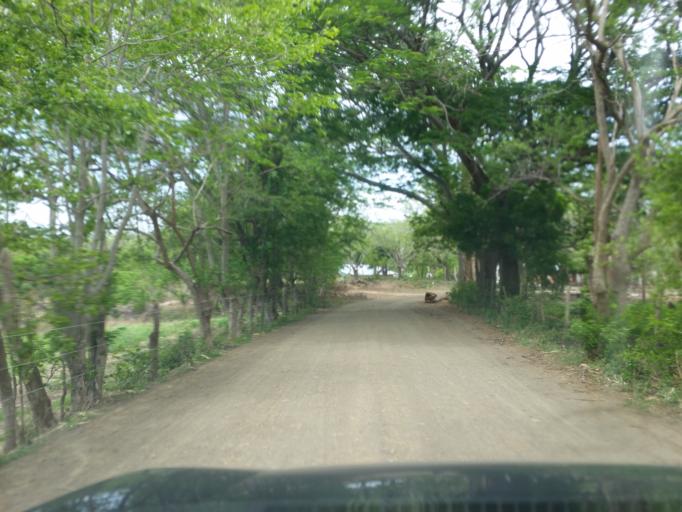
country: NI
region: Granada
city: Nandaime
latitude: 11.6394
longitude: -86.0043
